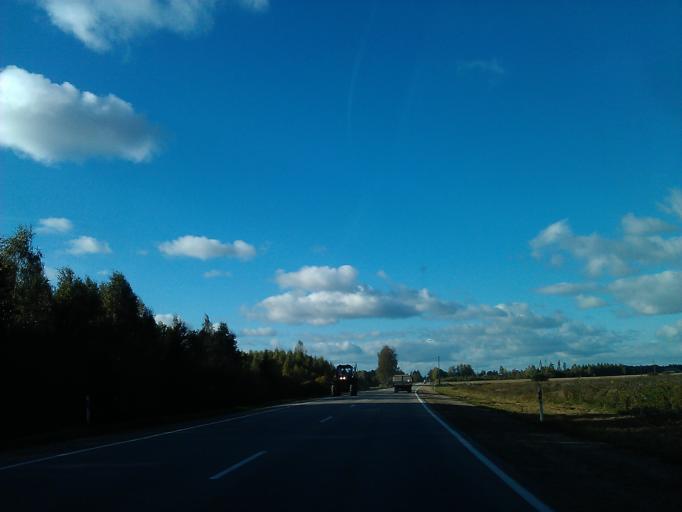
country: LV
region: Koknese
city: Koknese
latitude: 56.6257
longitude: 25.4659
